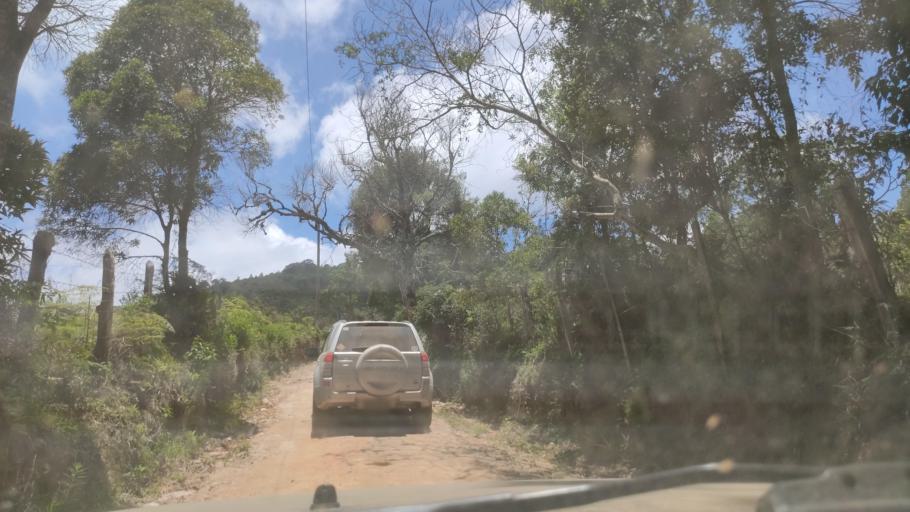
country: BR
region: Minas Gerais
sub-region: Cambui
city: Cambui
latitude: -22.6822
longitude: -45.9600
